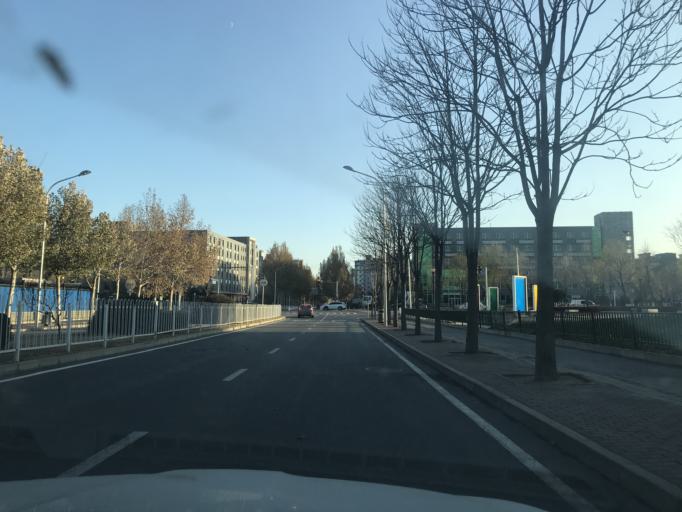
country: CN
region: Beijing
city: Xibeiwang
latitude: 40.0688
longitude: 116.2472
